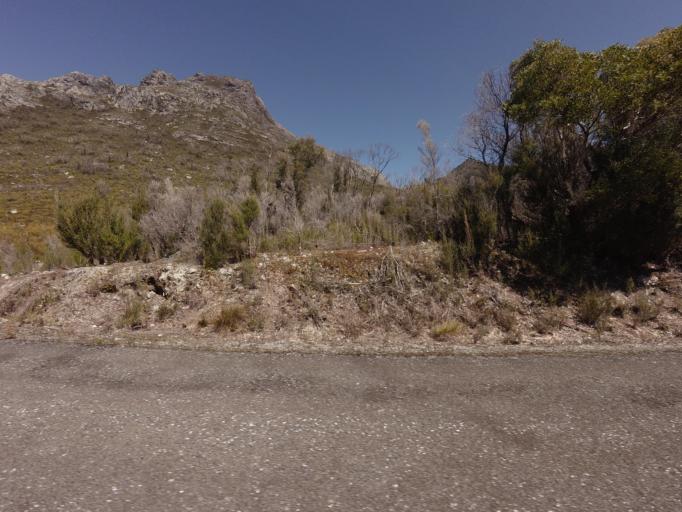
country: AU
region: Tasmania
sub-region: Huon Valley
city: Geeveston
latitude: -42.8616
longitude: 146.2203
